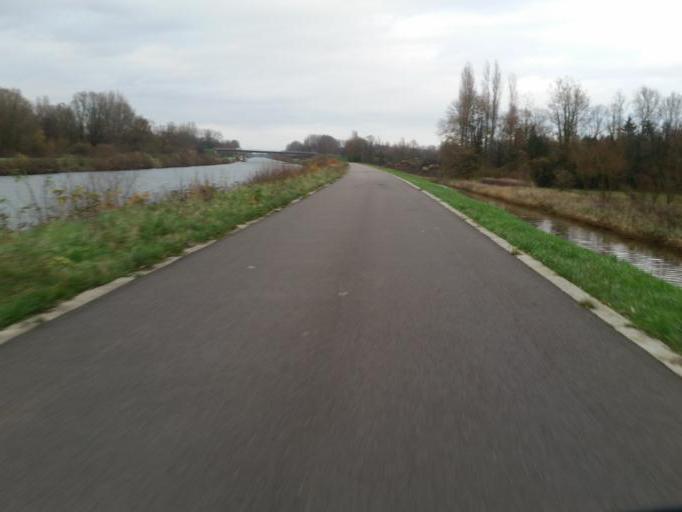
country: BE
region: Flanders
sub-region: Provincie Antwerpen
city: Lier
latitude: 51.1563
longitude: 4.6007
